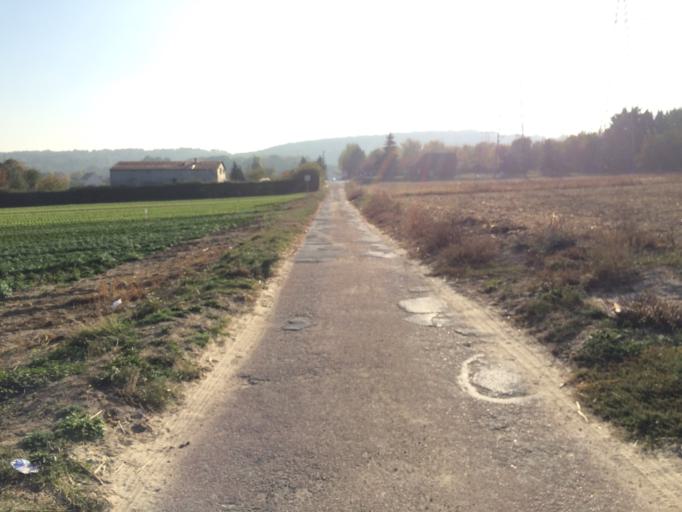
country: FR
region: Ile-de-France
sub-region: Departement de l'Essonne
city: Villebon-sur-Yvette
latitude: 48.6971
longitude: 2.2488
